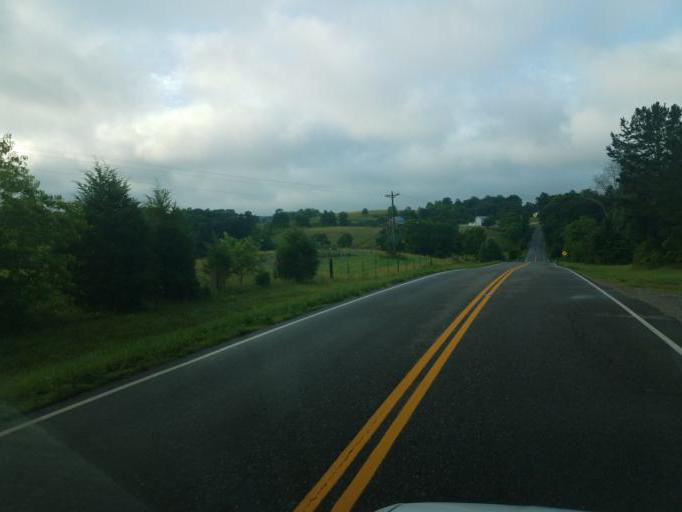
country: US
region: Ohio
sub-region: Jackson County
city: Oak Hill
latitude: 38.8086
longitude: -82.4002
